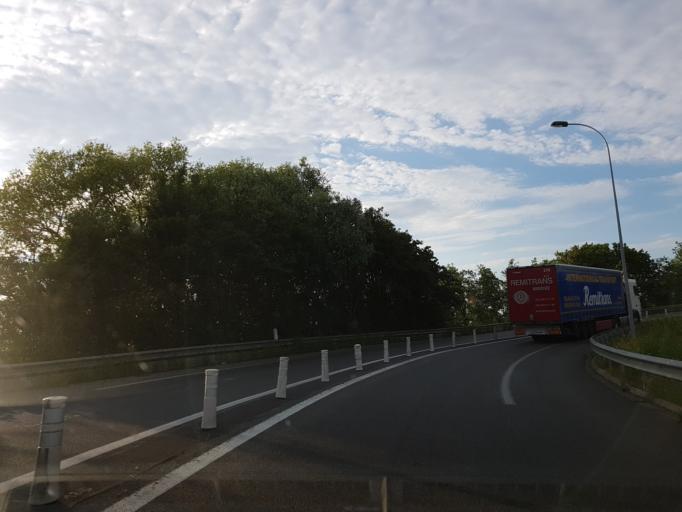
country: FR
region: Picardie
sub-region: Departement de l'Oise
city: Chevrieres
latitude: 49.3195
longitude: 2.6852
